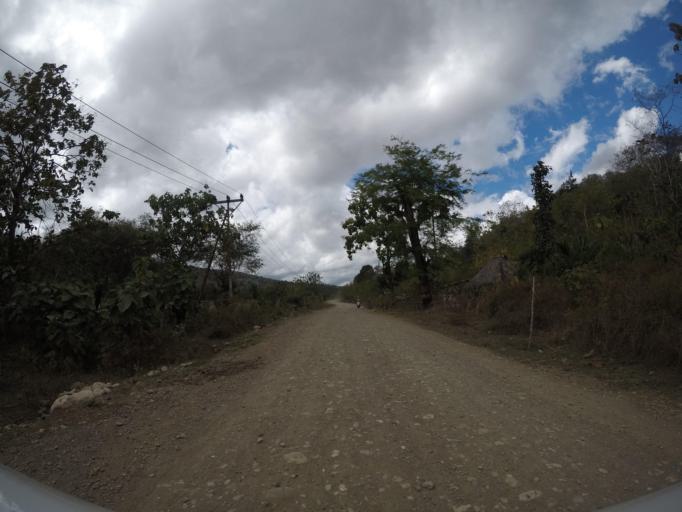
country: TL
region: Lautem
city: Lospalos
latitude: -8.4999
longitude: 126.8283
